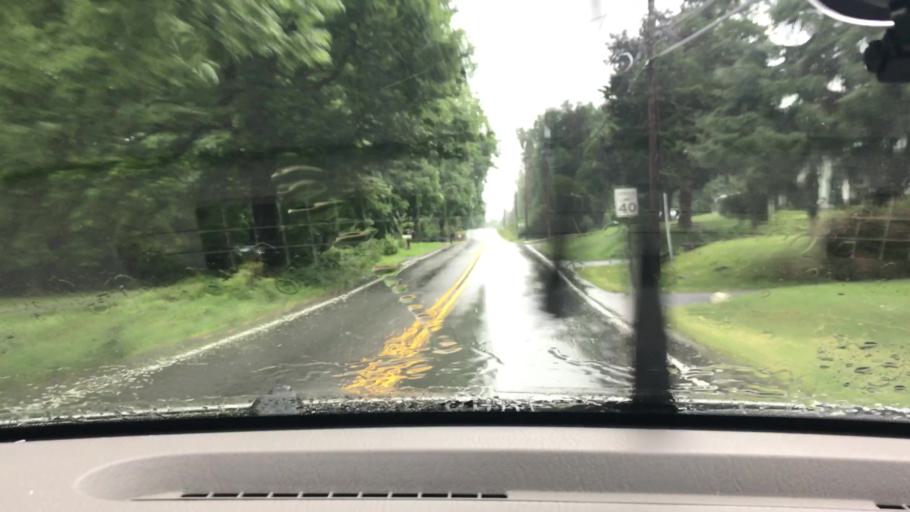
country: US
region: Pennsylvania
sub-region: Lancaster County
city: Elizabethtown
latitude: 40.1428
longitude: -76.6533
